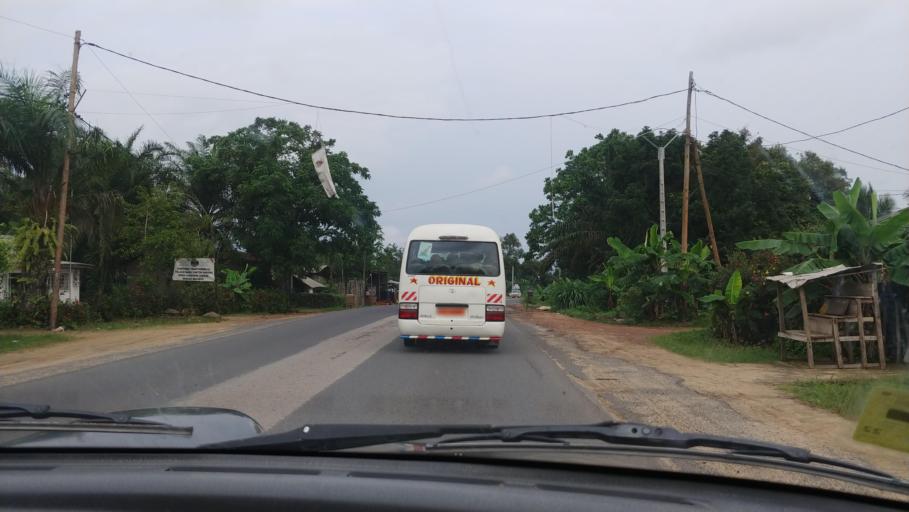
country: CM
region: Littoral
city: Dibombari
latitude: 4.1490
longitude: 9.5884
